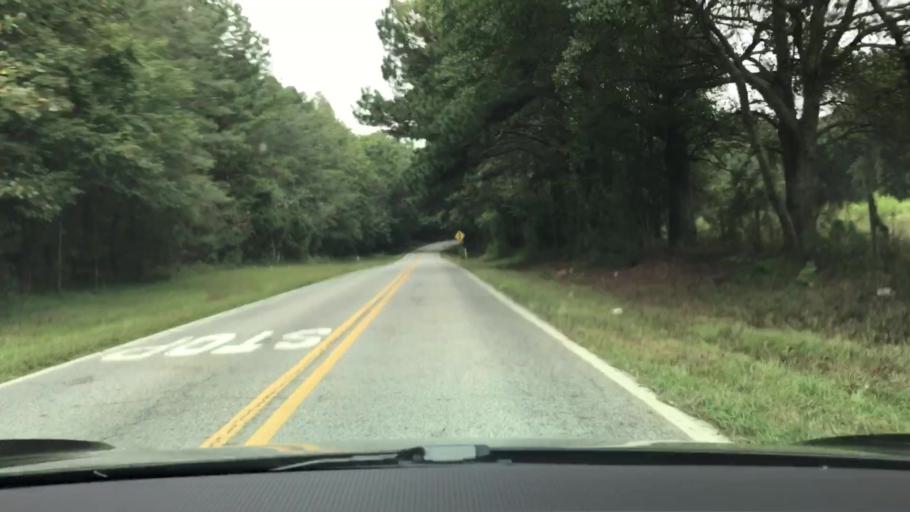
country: US
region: Georgia
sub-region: Barrow County
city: Auburn
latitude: 34.0334
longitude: -83.7978
